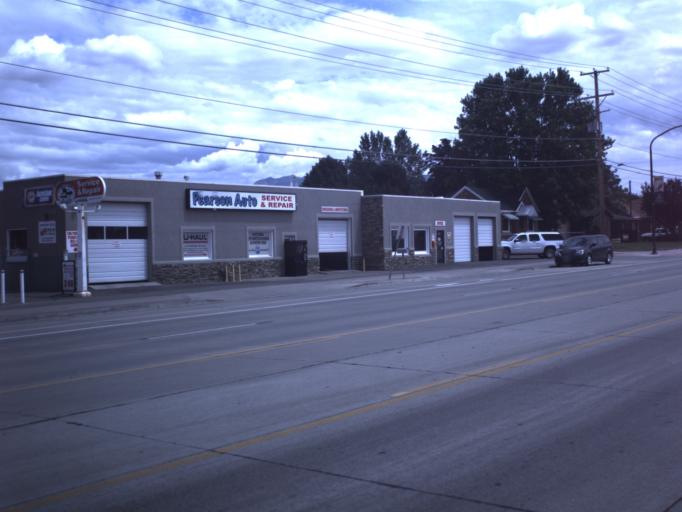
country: US
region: Utah
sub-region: Davis County
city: Syracuse
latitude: 41.0890
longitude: -112.0571
